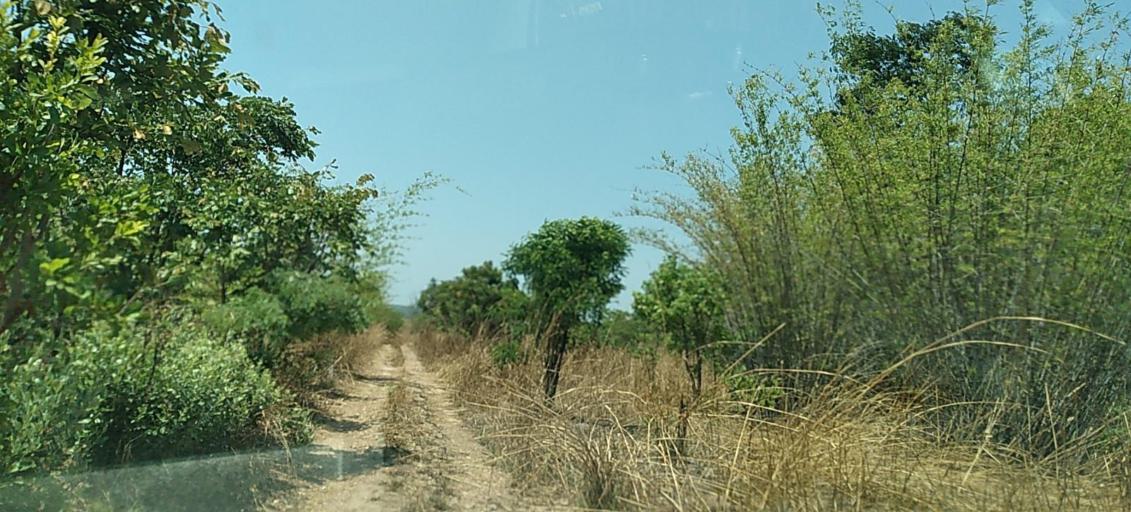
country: ZM
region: Copperbelt
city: Luanshya
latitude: -12.9784
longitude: 28.3296
